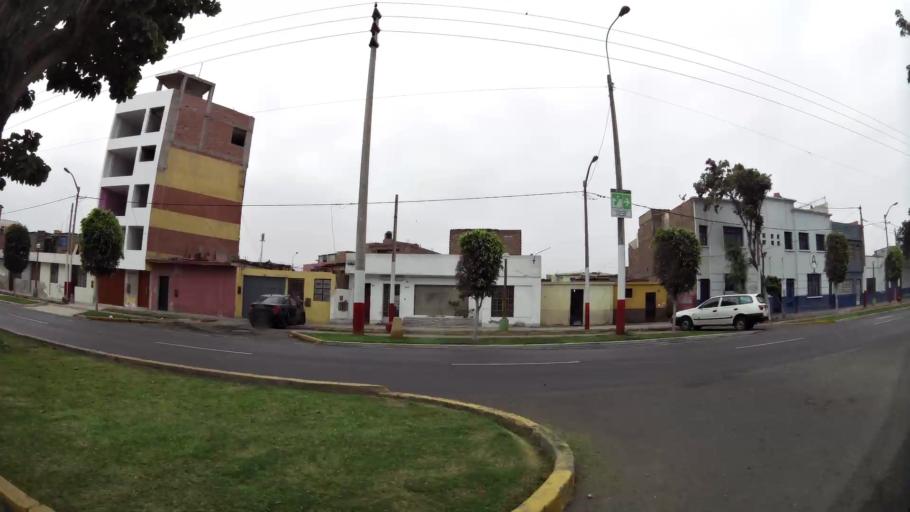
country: PE
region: Callao
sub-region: Callao
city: Callao
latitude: -12.0545
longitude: -77.1354
